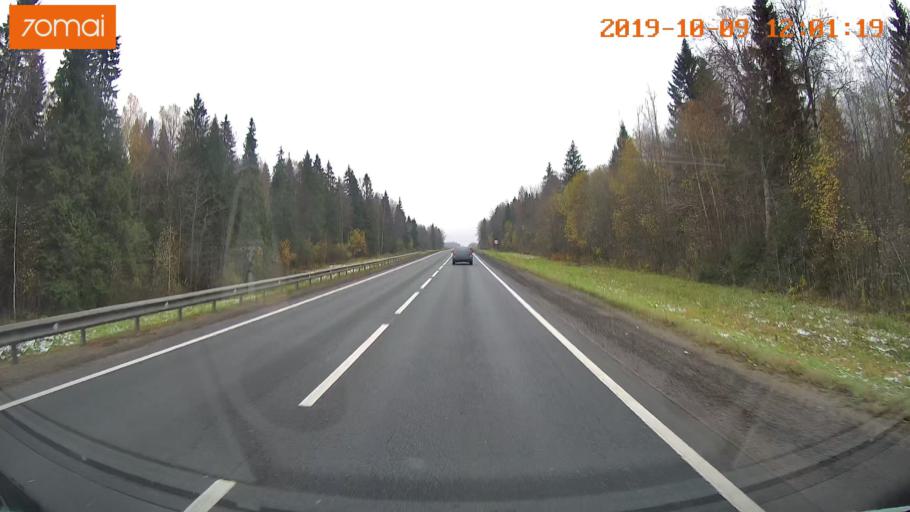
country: RU
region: Vologda
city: Gryazovets
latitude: 58.6894
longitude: 40.3029
